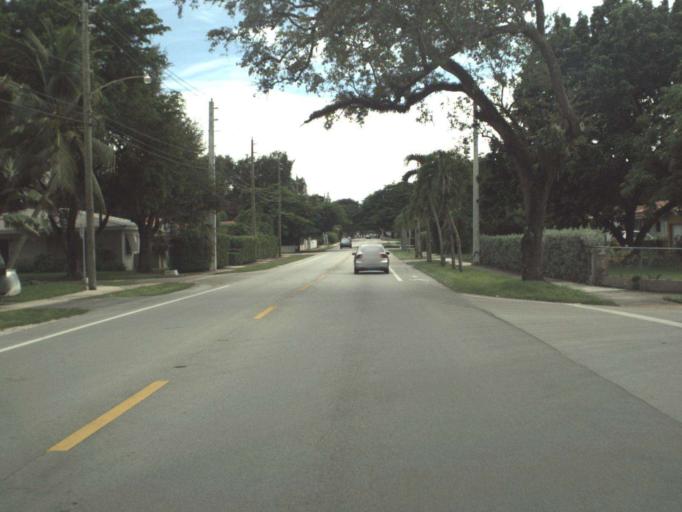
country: US
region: Florida
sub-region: Miami-Dade County
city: Coral Terrace
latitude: 25.7413
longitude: -80.2869
